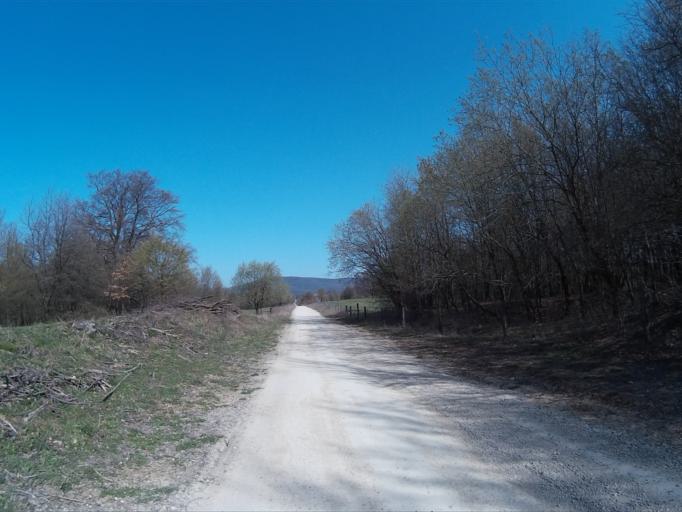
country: HU
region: Veszprem
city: Herend
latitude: 47.2086
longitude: 17.7912
